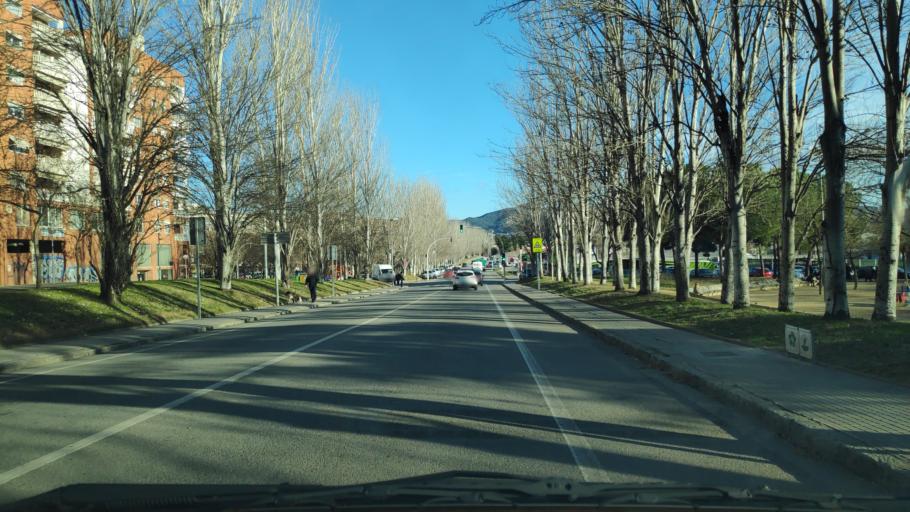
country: ES
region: Catalonia
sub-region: Provincia de Barcelona
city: Mollet del Valles
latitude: 41.5342
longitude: 2.2108
